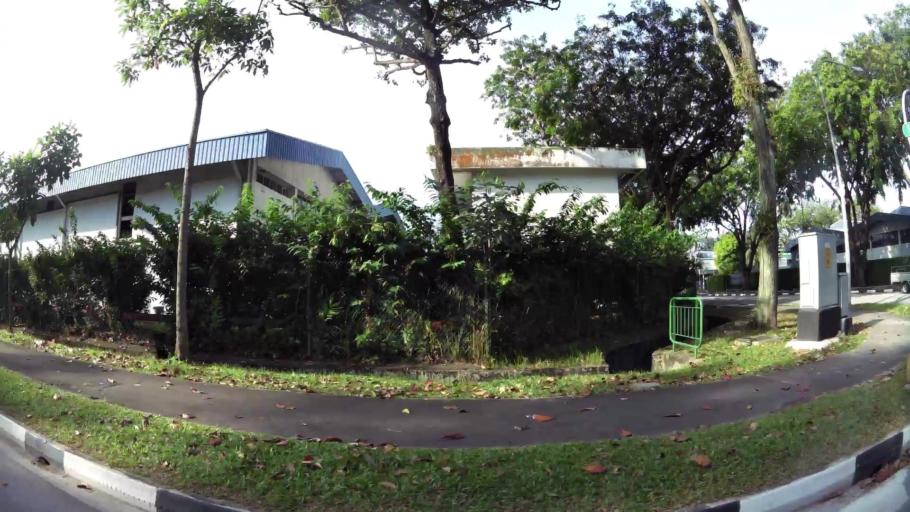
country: MY
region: Johor
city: Johor Bahru
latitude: 1.3265
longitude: 103.6558
